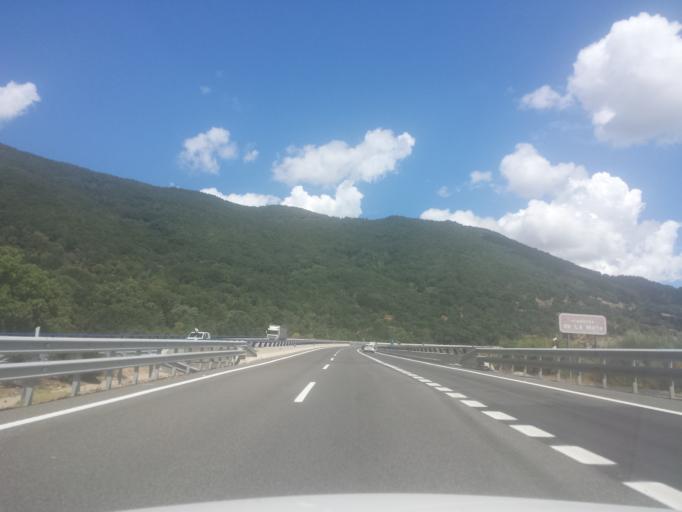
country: ES
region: Extremadura
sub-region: Provincia de Caceres
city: Banos de Montemayor
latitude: 40.3096
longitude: -5.8800
